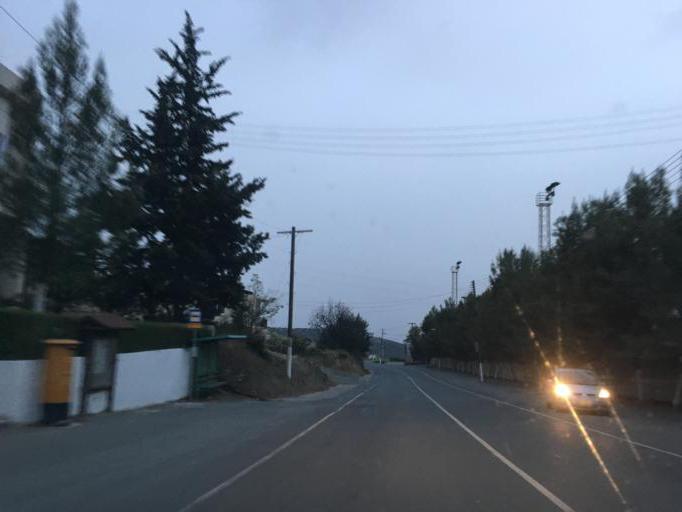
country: CY
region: Limassol
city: Parekklisha
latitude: 34.7367
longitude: 33.1615
